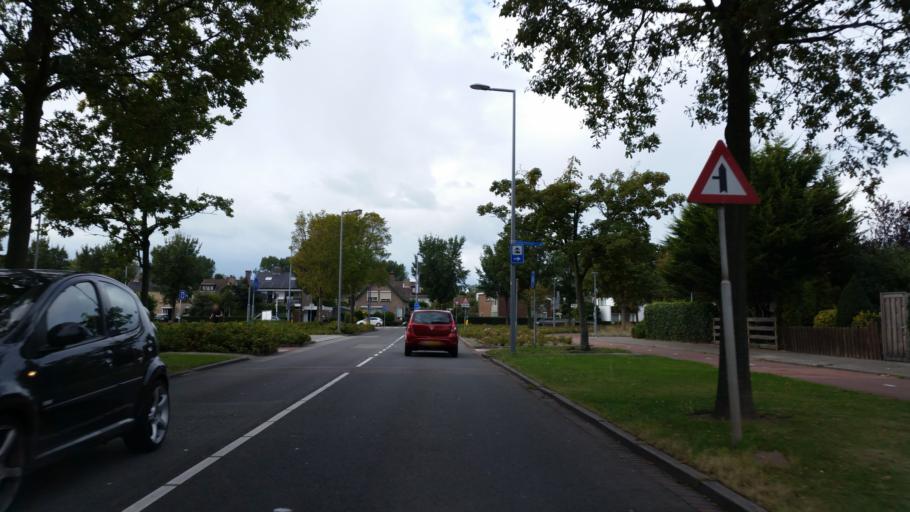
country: NL
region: South Holland
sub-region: Gemeente Rotterdam
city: Hoek van Holland
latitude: 51.9843
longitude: 4.1301
